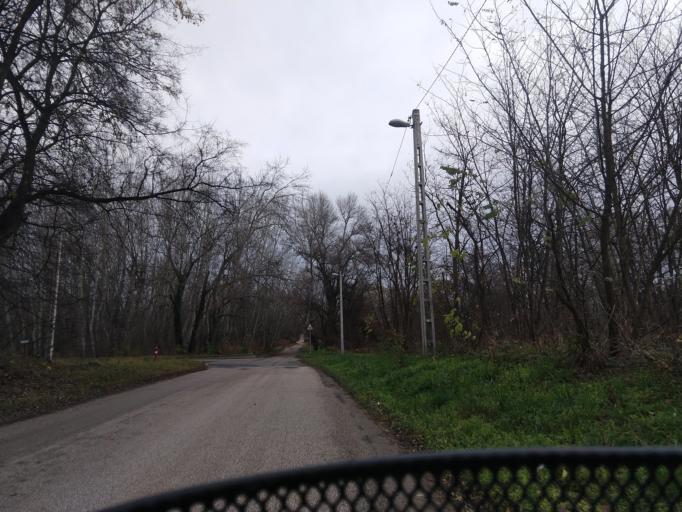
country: HU
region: Pest
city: Erdokertes
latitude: 47.6670
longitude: 19.2930
